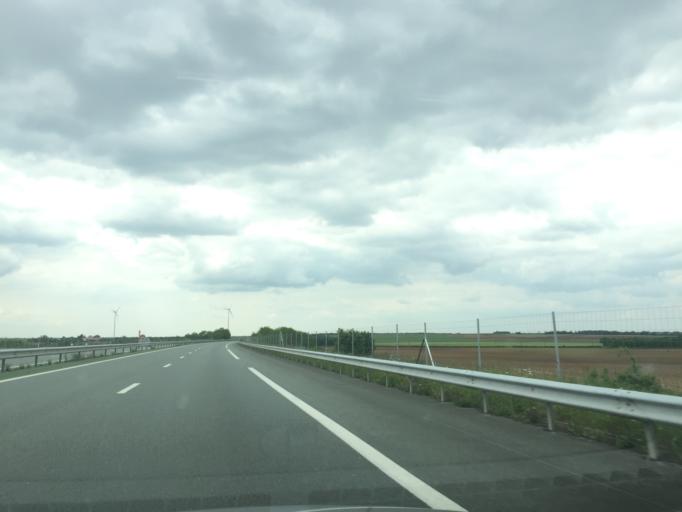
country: FR
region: Pays de la Loire
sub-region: Departement de la Vendee
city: Benet
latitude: 46.4046
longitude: -0.5892
